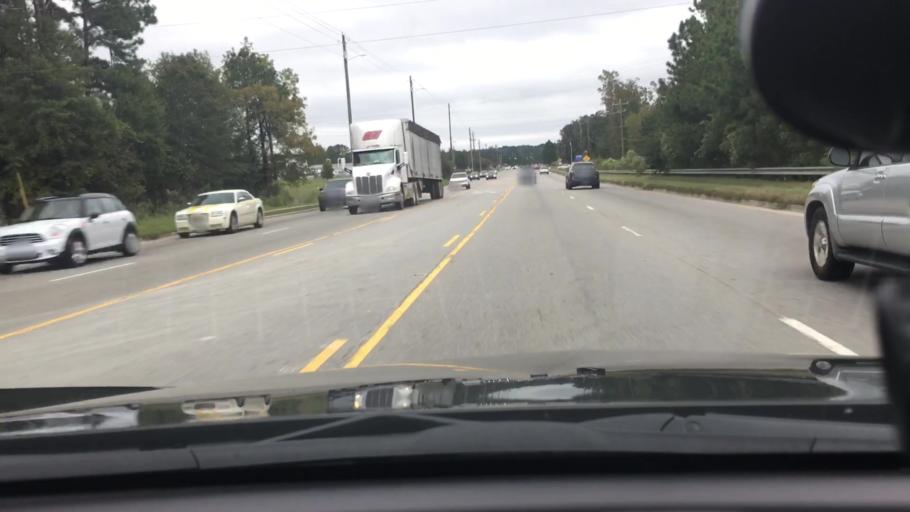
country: US
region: North Carolina
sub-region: Wake County
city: Apex
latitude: 35.7100
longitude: -78.8379
